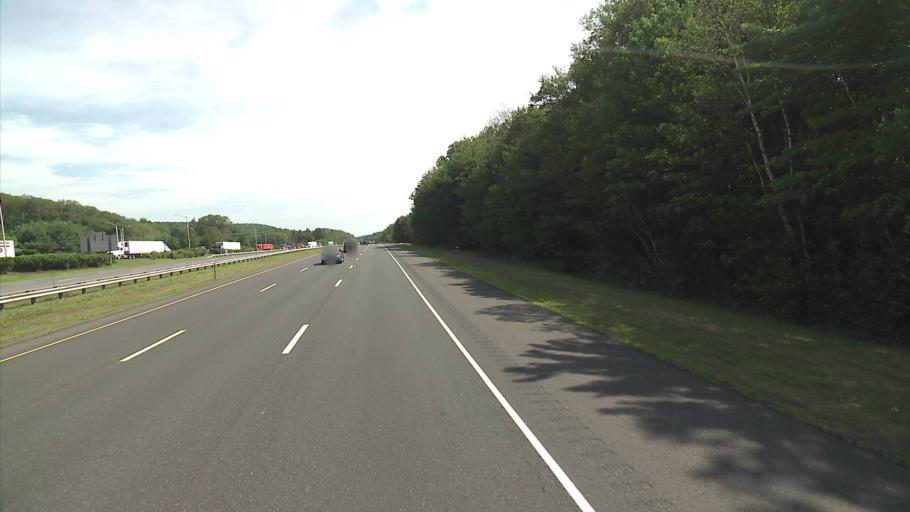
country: US
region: Massachusetts
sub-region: Hampden County
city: Holland
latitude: 41.9870
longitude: -72.1749
